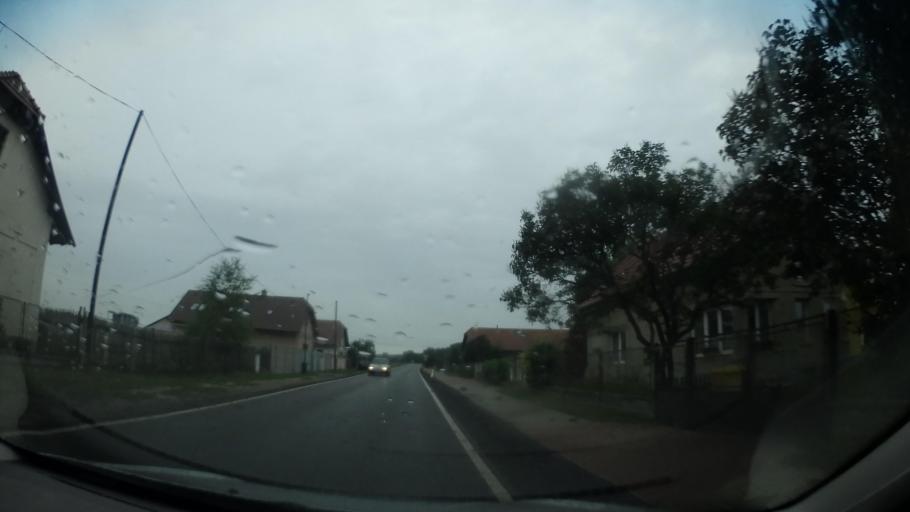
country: CZ
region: Central Bohemia
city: Milovice
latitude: 50.2396
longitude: 14.9532
